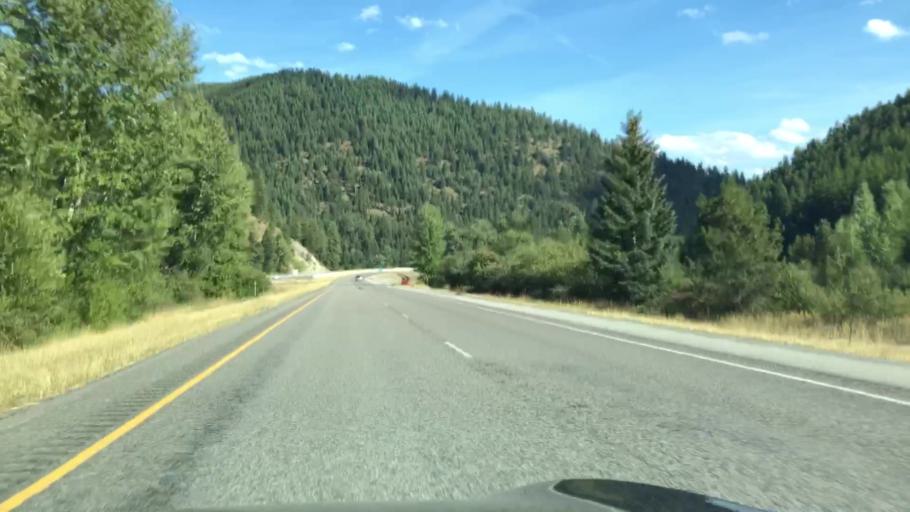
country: US
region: Montana
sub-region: Sanders County
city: Thompson Falls
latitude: 47.3566
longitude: -115.3007
